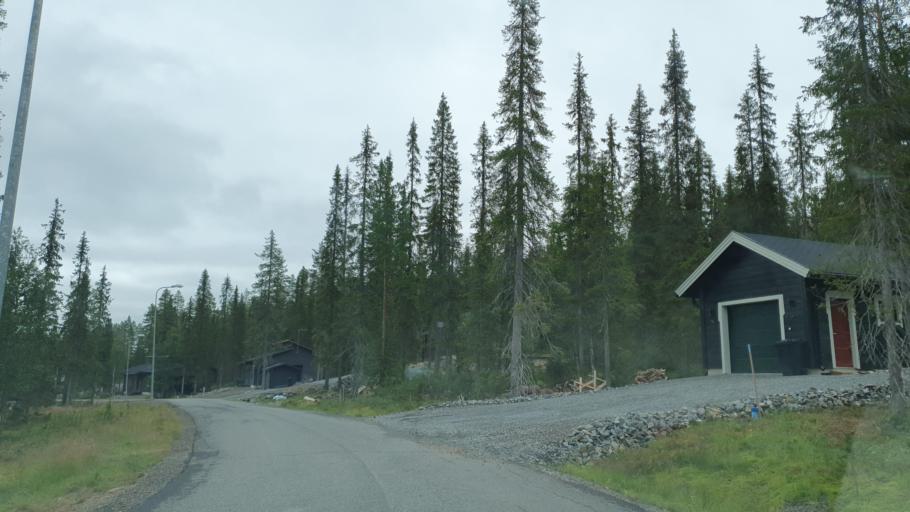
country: FI
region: Lapland
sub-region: Tunturi-Lappi
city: Kolari
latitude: 67.5912
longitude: 24.1720
